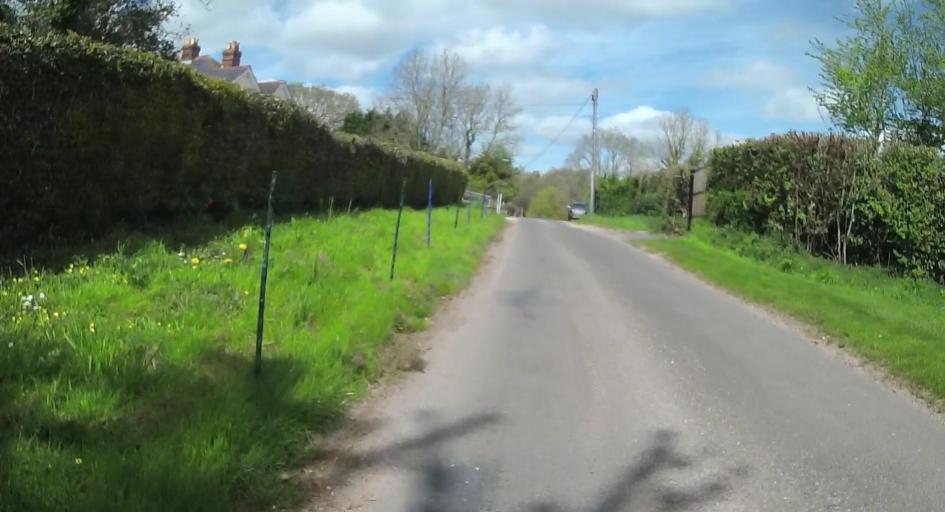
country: GB
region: England
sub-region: Hampshire
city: East Dean
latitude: 51.0635
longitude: -1.5322
